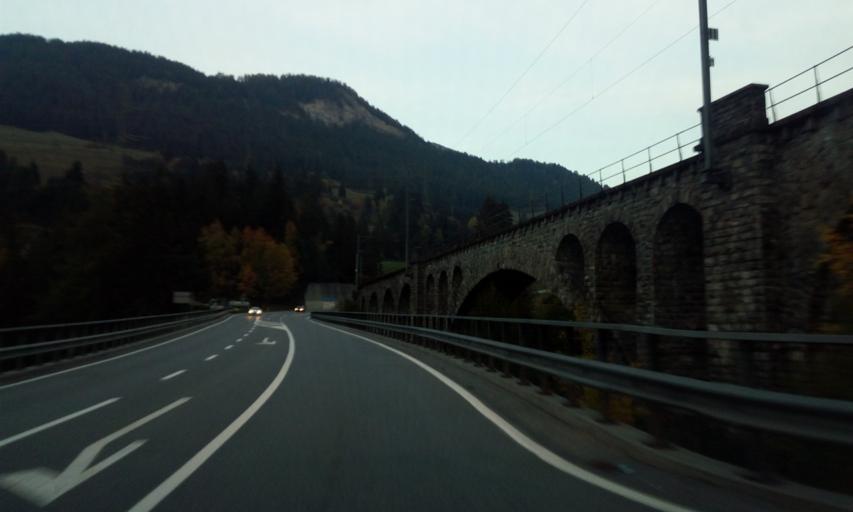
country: CH
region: Grisons
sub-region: Albula District
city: Tiefencastel
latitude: 46.6791
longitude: 9.5296
